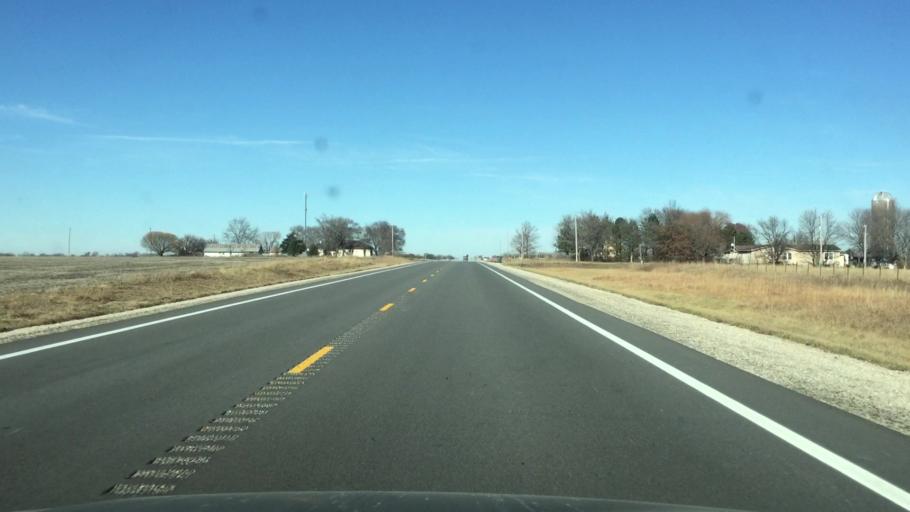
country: US
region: Kansas
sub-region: Anderson County
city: Garnett
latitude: 38.3816
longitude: -95.2488
